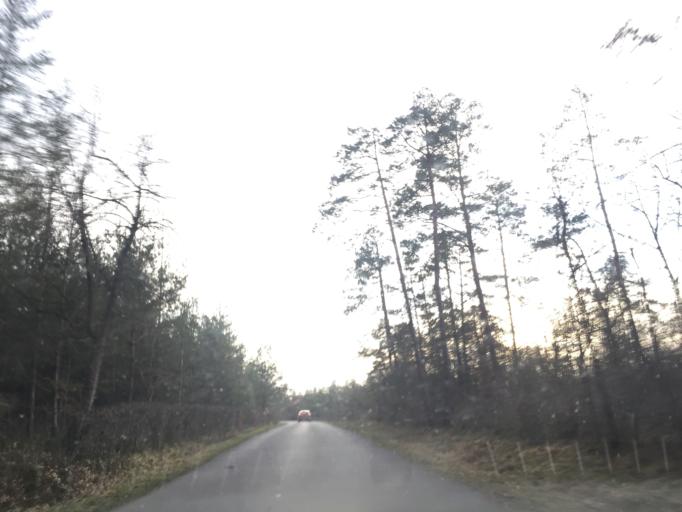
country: BE
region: Wallonia
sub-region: Province du Luxembourg
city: Durbuy
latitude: 50.3168
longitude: 5.4879
